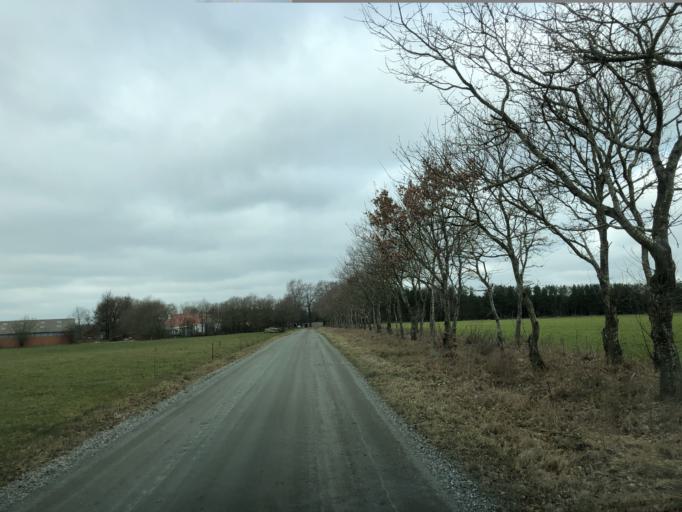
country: DK
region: South Denmark
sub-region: Billund Kommune
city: Billund
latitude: 55.7726
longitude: 9.1406
